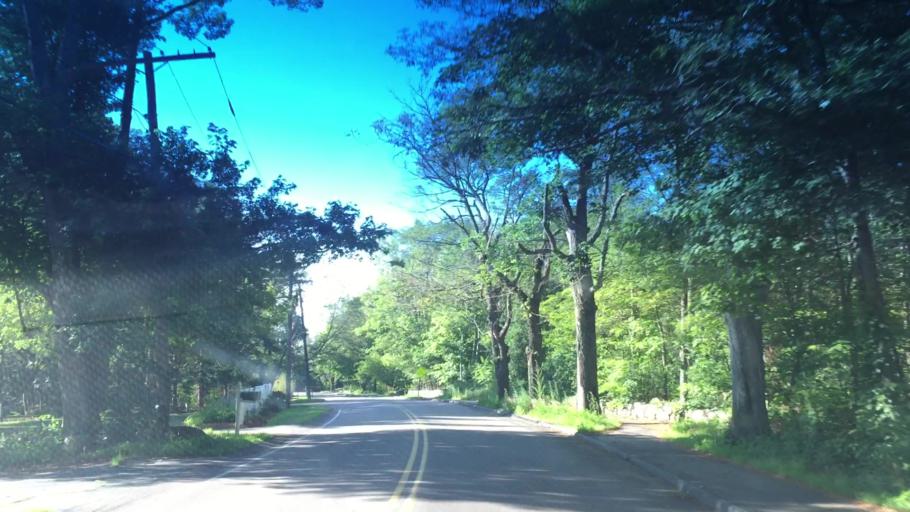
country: US
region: Massachusetts
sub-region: Norfolk County
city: Millis-Clicquot
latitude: 42.1455
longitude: -71.3580
